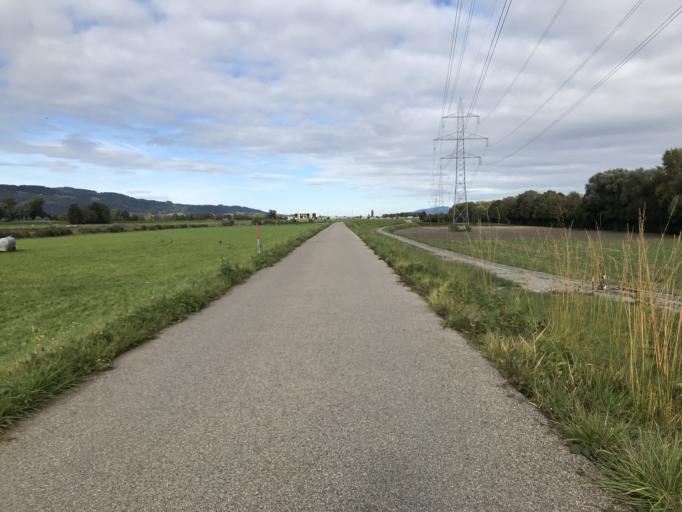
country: AT
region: Vorarlberg
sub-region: Politischer Bezirk Feldkirch
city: Koblach
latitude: 47.3433
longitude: 9.6003
